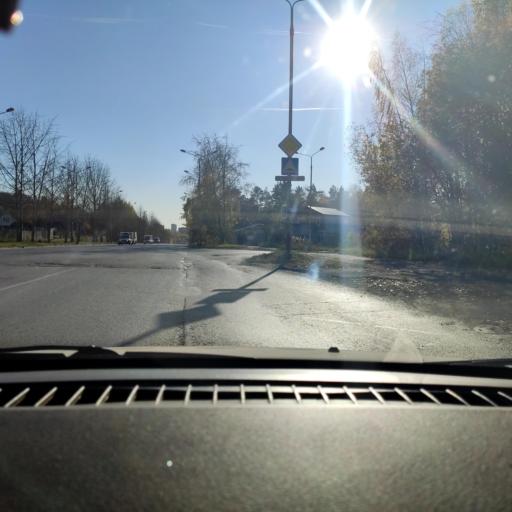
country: RU
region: Perm
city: Perm
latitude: 58.0802
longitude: 56.3733
